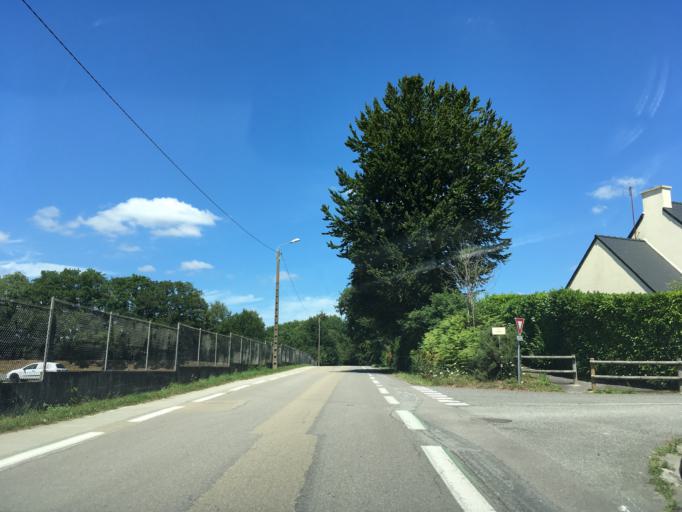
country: FR
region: Brittany
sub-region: Departement du Finistere
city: Quimper
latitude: 47.9773
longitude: -4.0735
